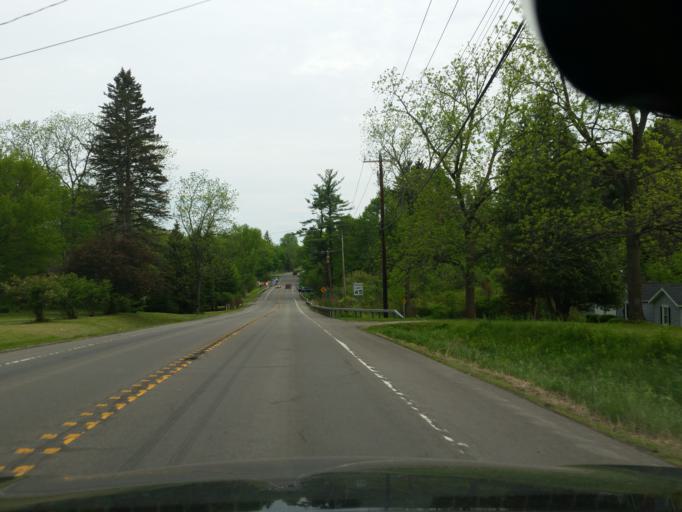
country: US
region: New York
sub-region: Chautauqua County
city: Lakewood
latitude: 42.1341
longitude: -79.3966
